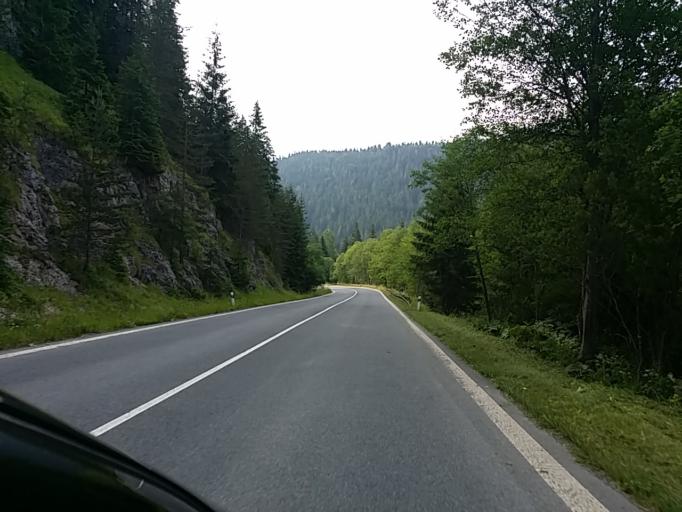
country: SK
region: Kosicky
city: Dobsina
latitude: 48.8824
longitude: 20.2515
